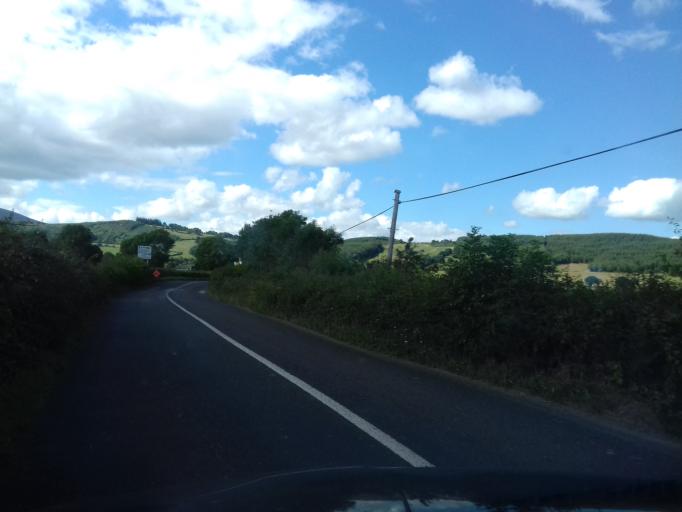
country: IE
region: Munster
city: Carrick-on-Suir
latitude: 52.3919
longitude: -7.4691
